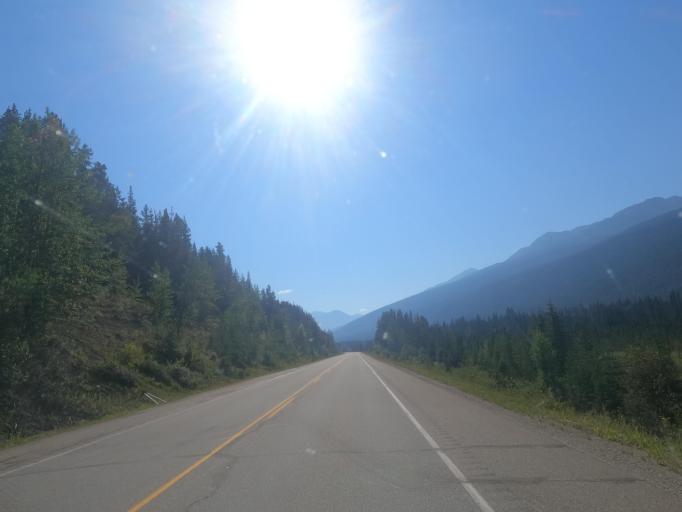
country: CA
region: Alberta
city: Jasper Park Lodge
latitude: 52.8907
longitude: -118.7286
